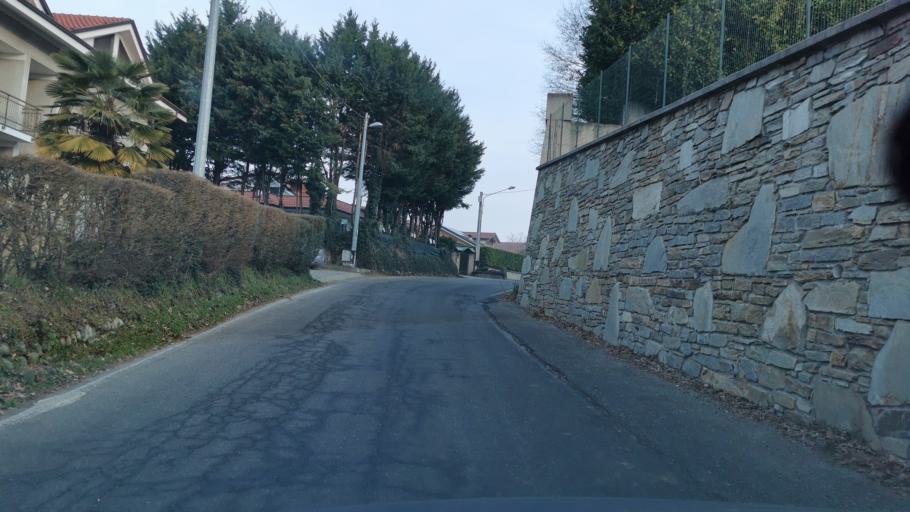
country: IT
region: Piedmont
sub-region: Provincia di Torino
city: Cuceglio
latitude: 45.3525
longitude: 7.8153
